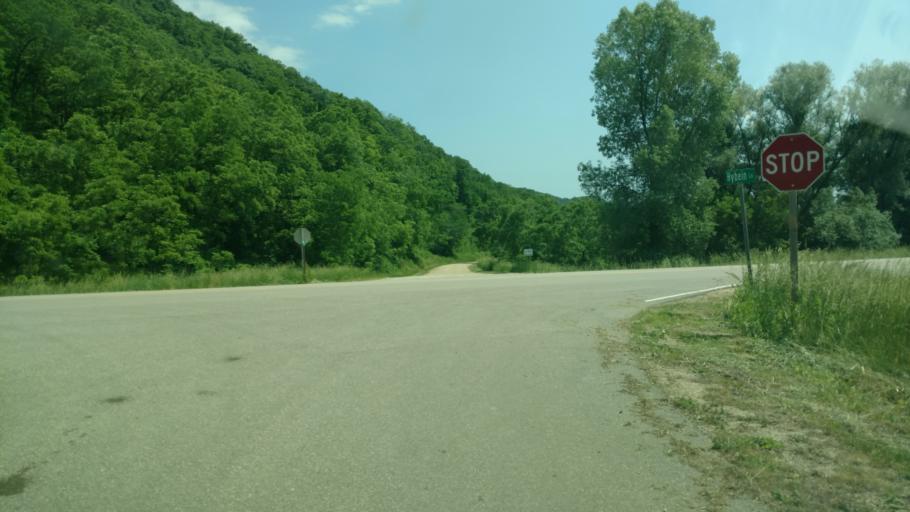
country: US
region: Wisconsin
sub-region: Vernon County
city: Westby
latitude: 43.5501
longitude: -90.6650
